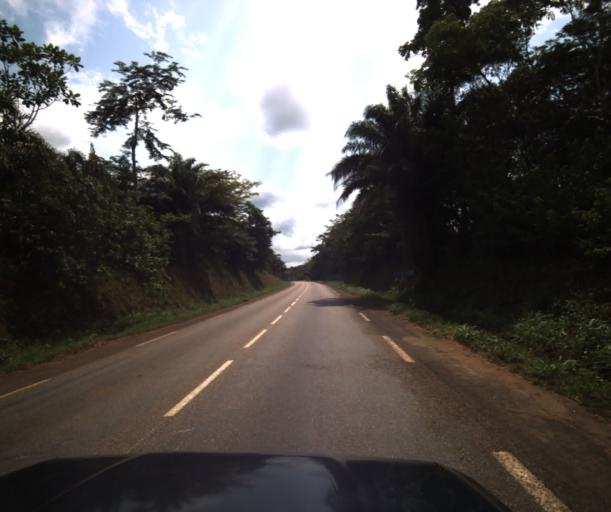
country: CM
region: Centre
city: Eseka
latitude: 3.8720
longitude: 10.6214
